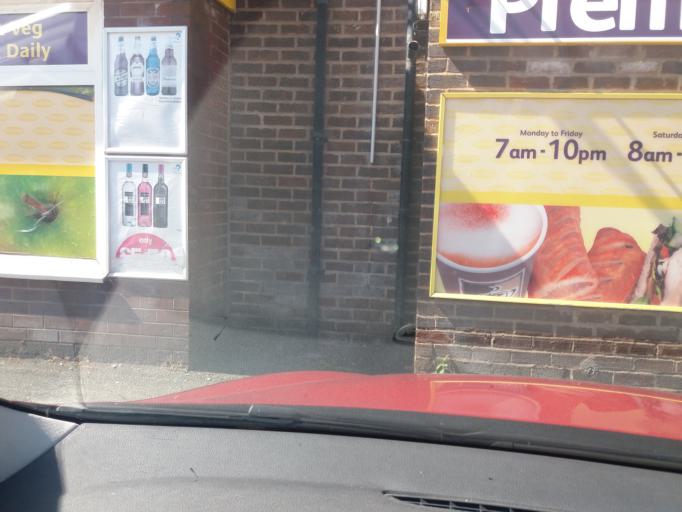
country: GB
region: England
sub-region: Lancashire
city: Preston
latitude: 53.7969
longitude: -2.7140
